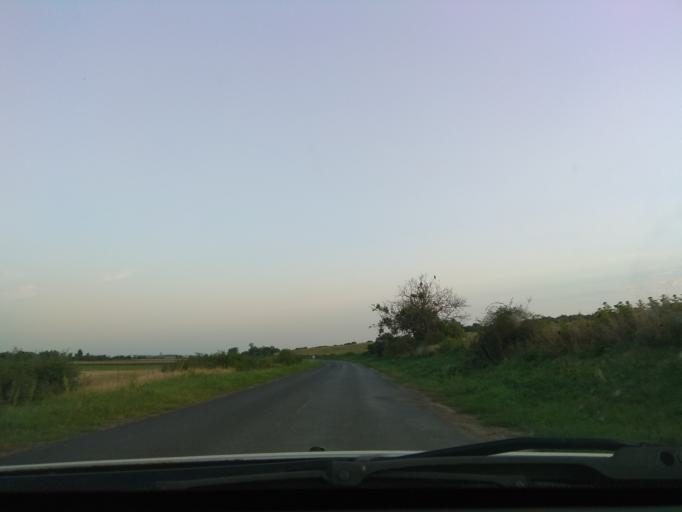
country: HU
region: Borsod-Abauj-Zemplen
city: Tallya
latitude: 48.2043
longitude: 21.2112
